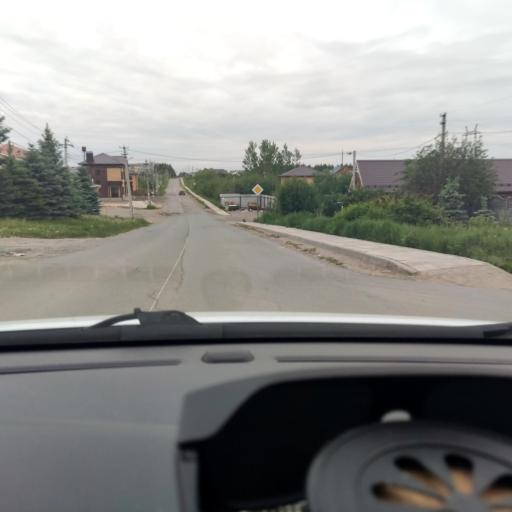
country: RU
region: Tatarstan
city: Vysokaya Gora
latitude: 55.9135
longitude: 49.3292
